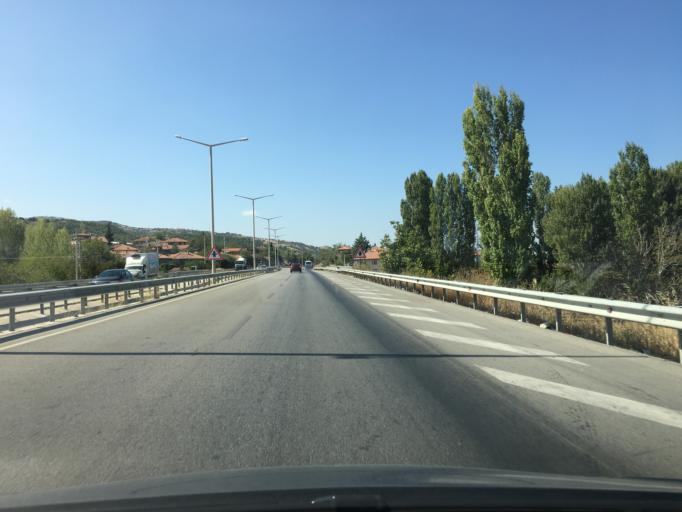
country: TR
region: Burdur
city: Burdur
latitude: 37.7603
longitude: 30.3445
